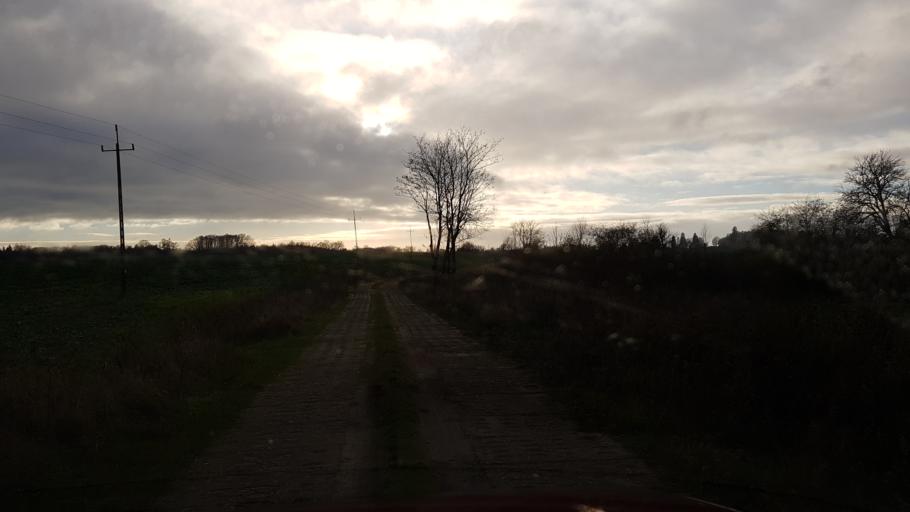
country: PL
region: West Pomeranian Voivodeship
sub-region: Powiat szczecinecki
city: Grzmiaca
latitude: 53.9924
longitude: 16.4136
